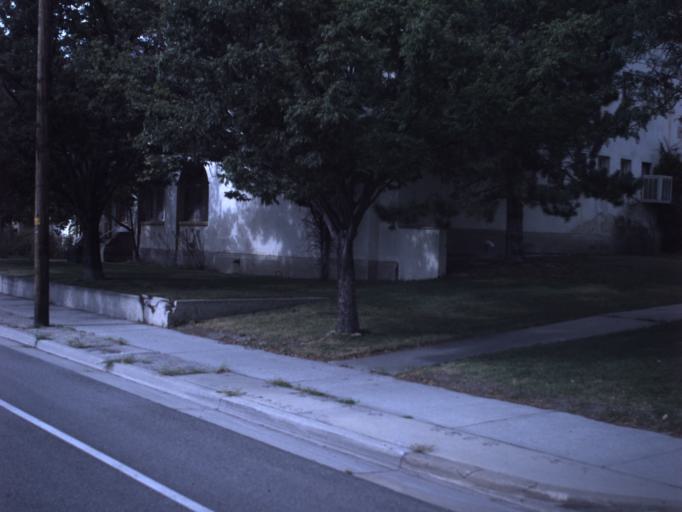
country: US
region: Utah
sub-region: Salt Lake County
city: Salt Lake City
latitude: 40.7884
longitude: -111.8999
